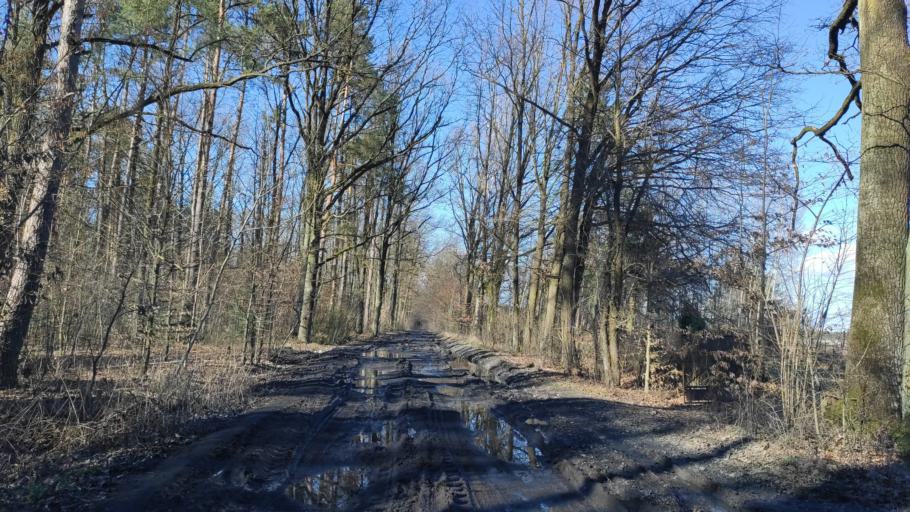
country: PL
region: Masovian Voivodeship
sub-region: Powiat radomski
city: Jedlnia-Letnisko
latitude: 51.4533
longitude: 21.3252
